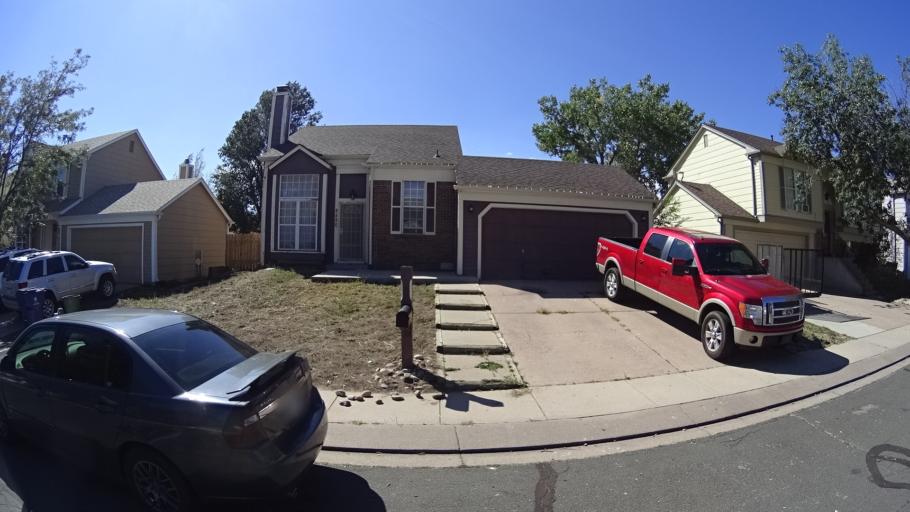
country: US
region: Colorado
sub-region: El Paso County
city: Stratmoor
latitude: 38.7950
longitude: -104.7384
